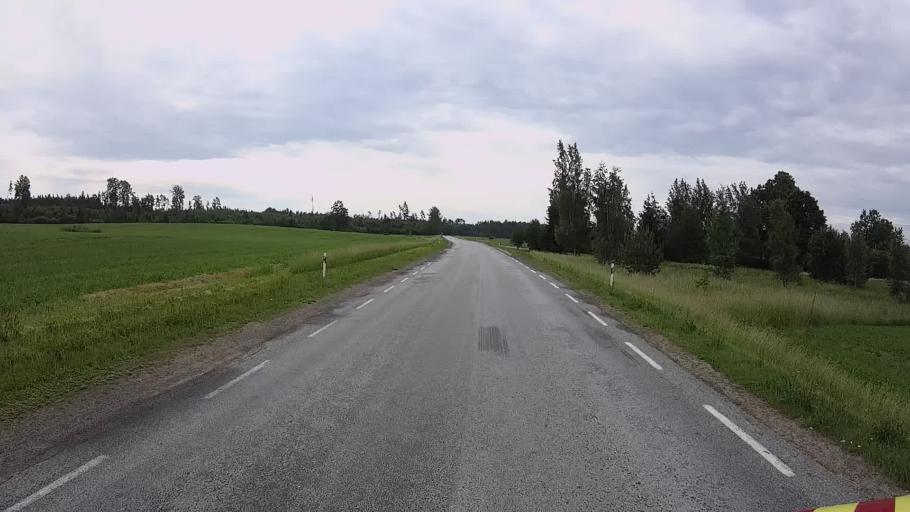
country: EE
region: Viljandimaa
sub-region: Karksi vald
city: Karksi-Nuia
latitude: 58.2294
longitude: 25.6038
